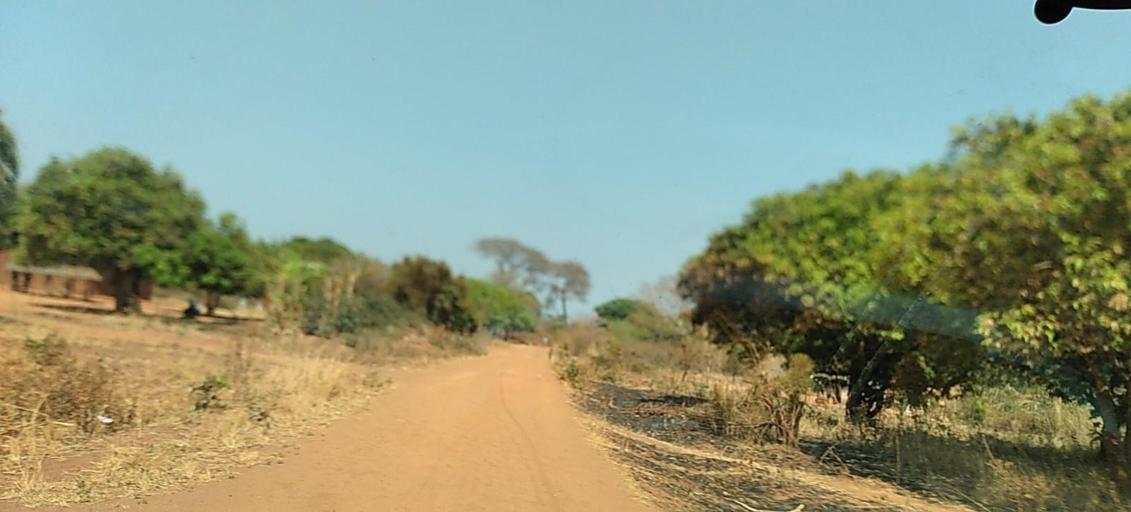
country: ZM
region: North-Western
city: Kasempa
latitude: -13.3896
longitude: 25.6774
